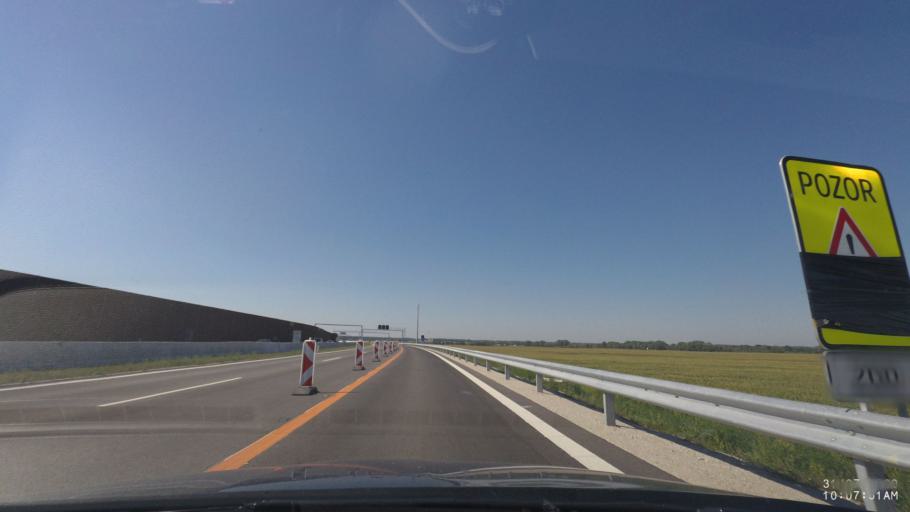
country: SK
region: Bratislavsky
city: Dunajska Luzna
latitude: 48.1052
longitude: 17.2169
